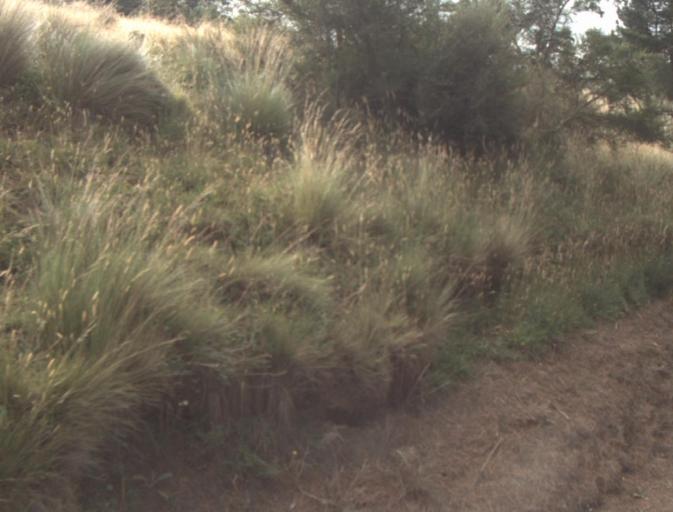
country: AU
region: Tasmania
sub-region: Dorset
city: Scottsdale
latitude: -41.3570
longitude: 147.4592
